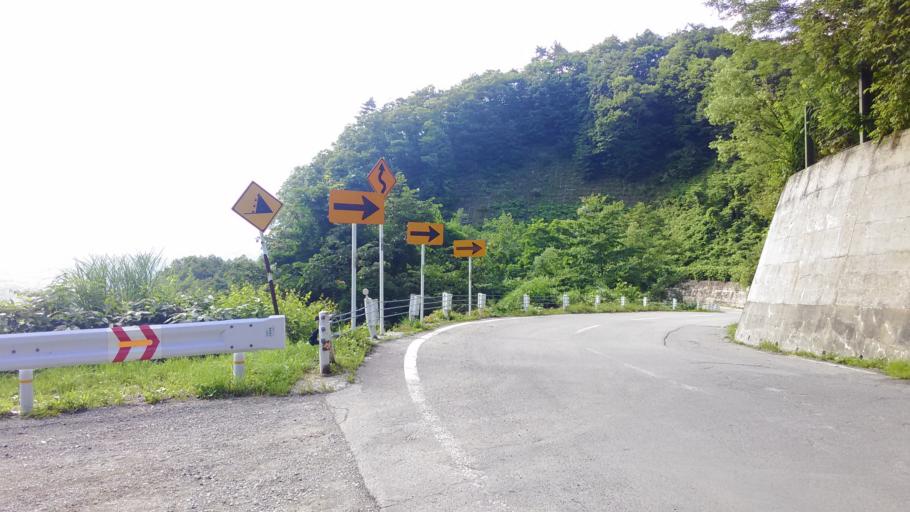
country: JP
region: Nagano
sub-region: Kitaazumi Gun
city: Hakuba
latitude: 36.6587
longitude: 137.8977
